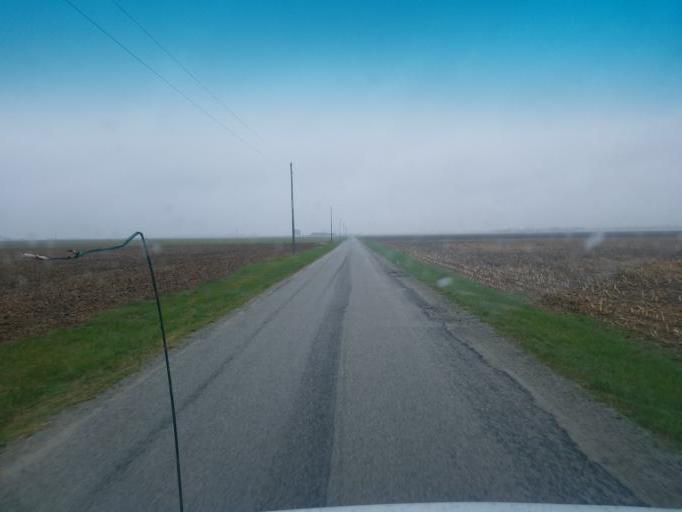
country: US
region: Ohio
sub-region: Wood County
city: North Baltimore
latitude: 41.2684
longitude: -83.6379
